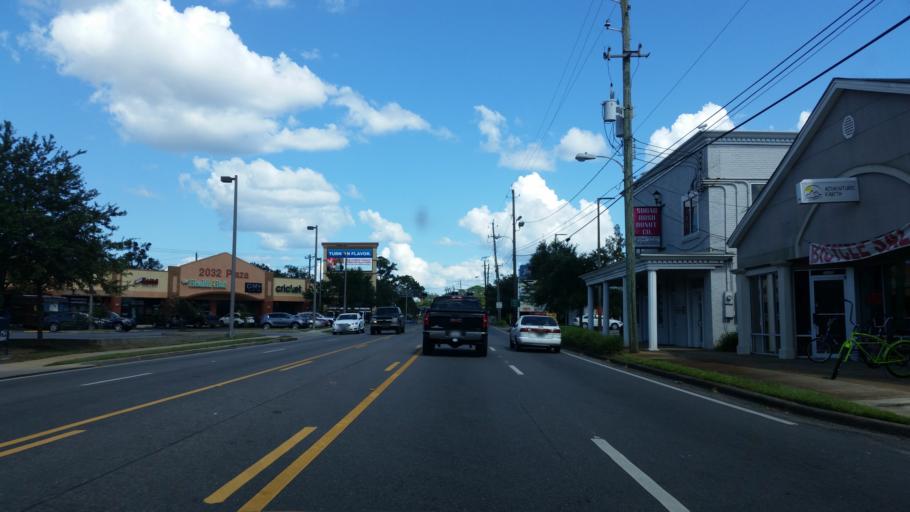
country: US
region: Alabama
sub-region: Mobile County
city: Mobile
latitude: 30.6764
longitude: -88.0899
